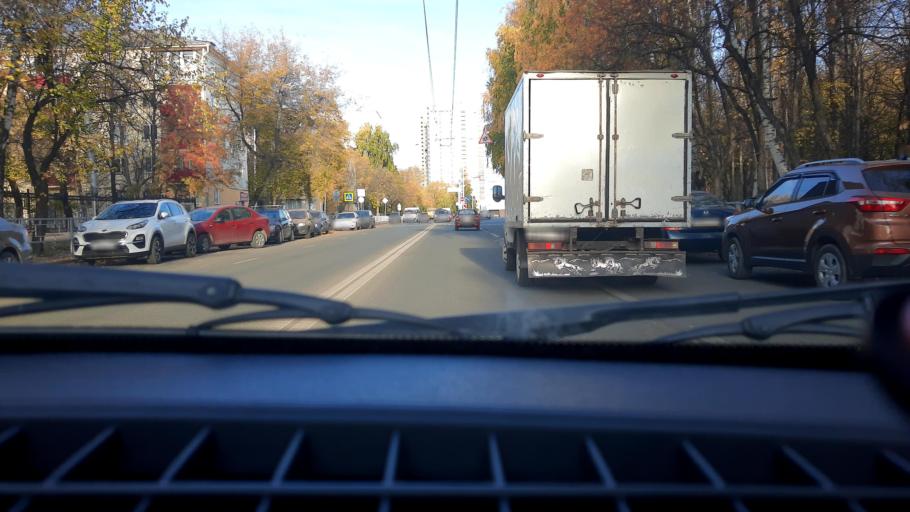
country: RU
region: Bashkortostan
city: Ufa
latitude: 54.7624
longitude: 56.0065
